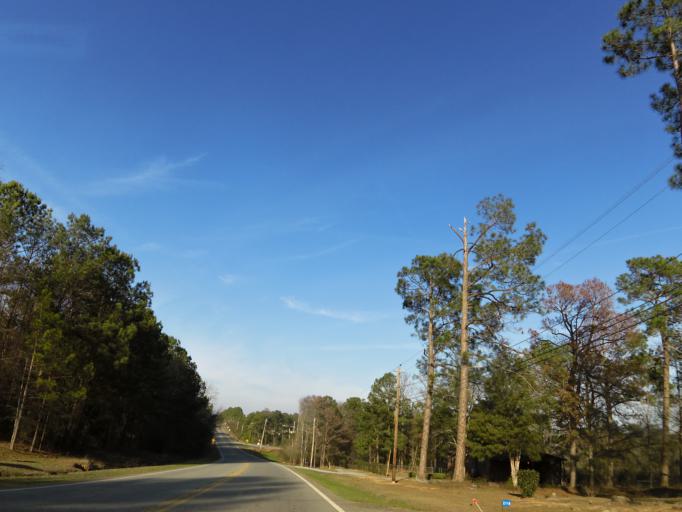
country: US
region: Georgia
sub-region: Stewart County
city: Richland
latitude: 32.0906
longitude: -84.6504
